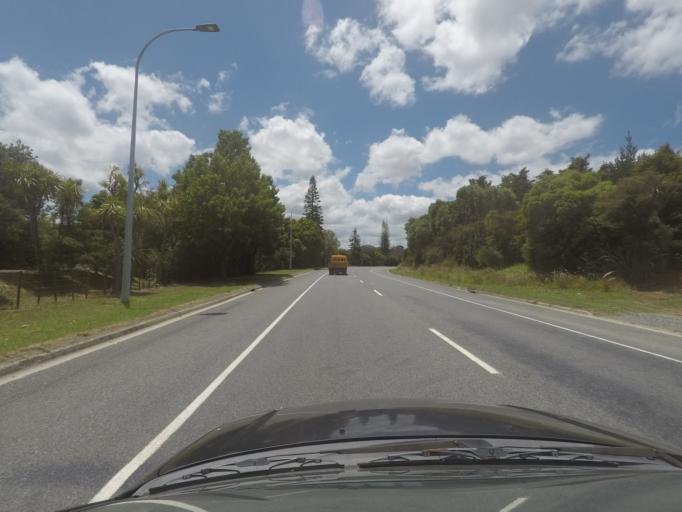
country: NZ
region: Northland
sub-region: Whangarei
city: Whangarei
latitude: -35.7479
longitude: 174.3208
